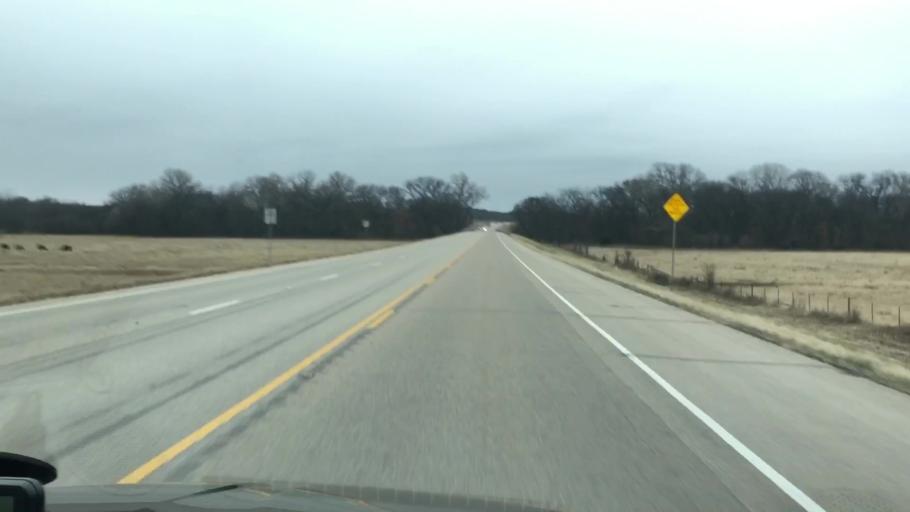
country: US
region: Texas
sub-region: Hamilton County
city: Hamilton
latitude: 31.7849
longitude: -98.1221
